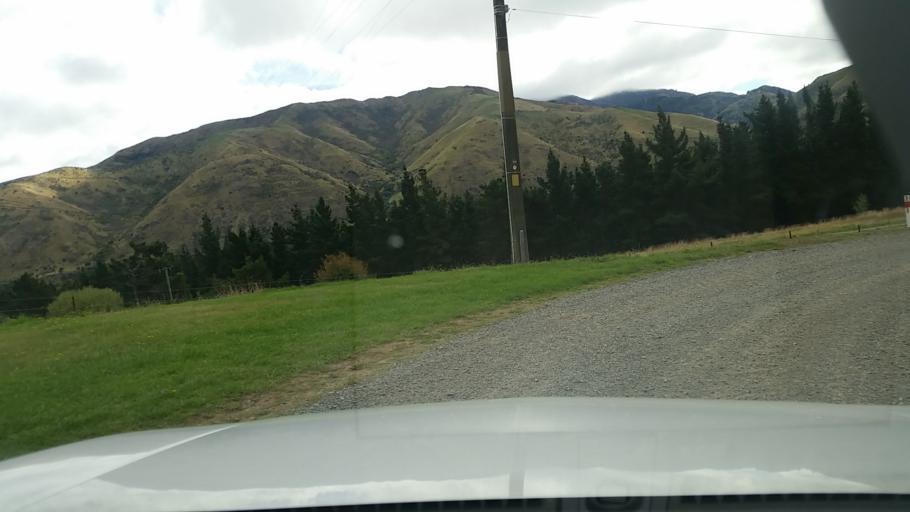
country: NZ
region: Marlborough
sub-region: Marlborough District
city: Blenheim
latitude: -41.6956
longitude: 173.9478
